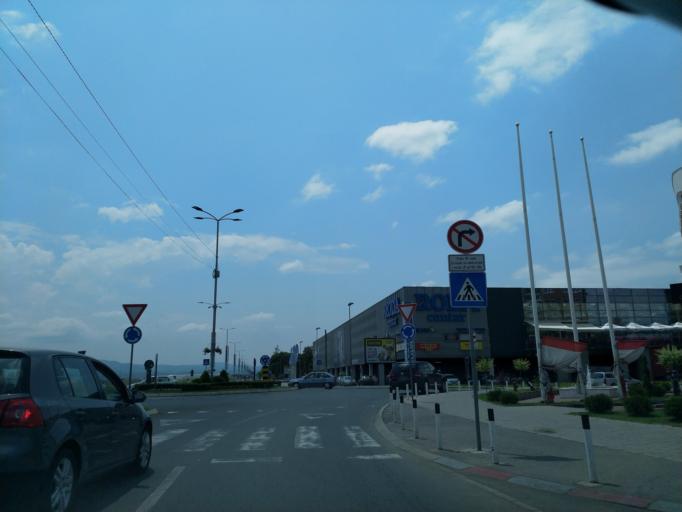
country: RS
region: Central Serbia
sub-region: Rasinski Okrug
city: Krusevac
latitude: 43.5693
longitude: 21.3372
